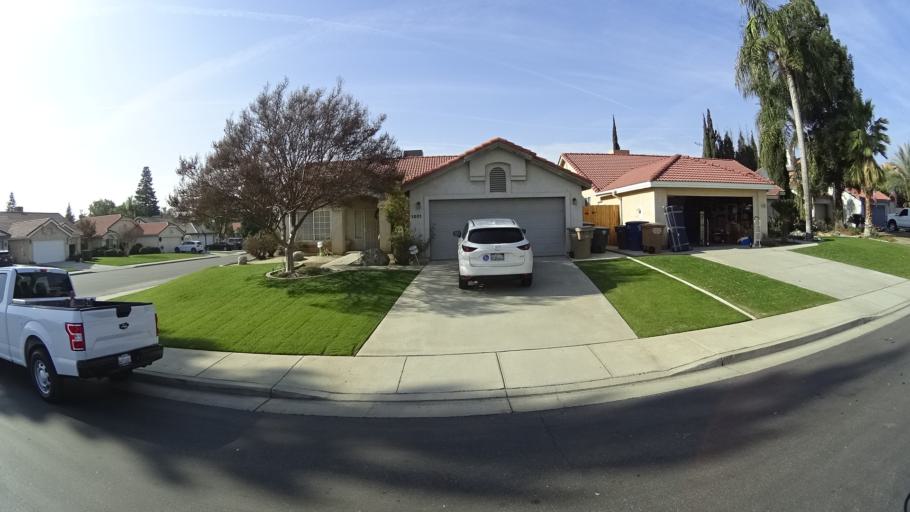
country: US
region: California
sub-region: Kern County
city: Greenacres
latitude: 35.3672
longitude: -119.0993
